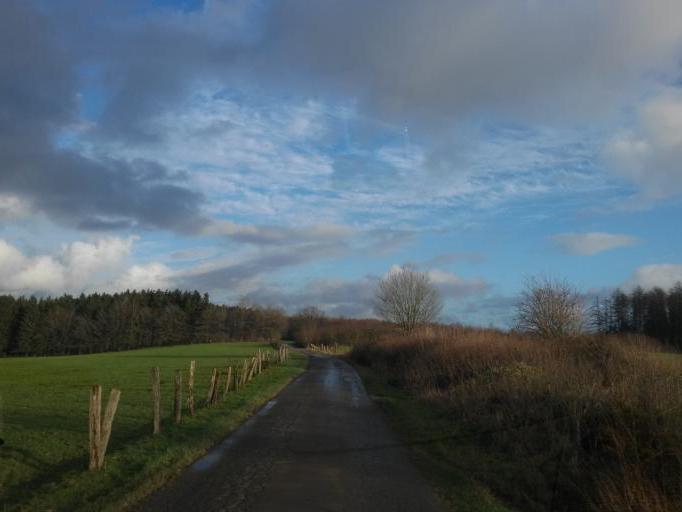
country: BE
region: Wallonia
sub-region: Province du Luxembourg
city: Neufchateau
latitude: 49.8238
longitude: 5.4423
